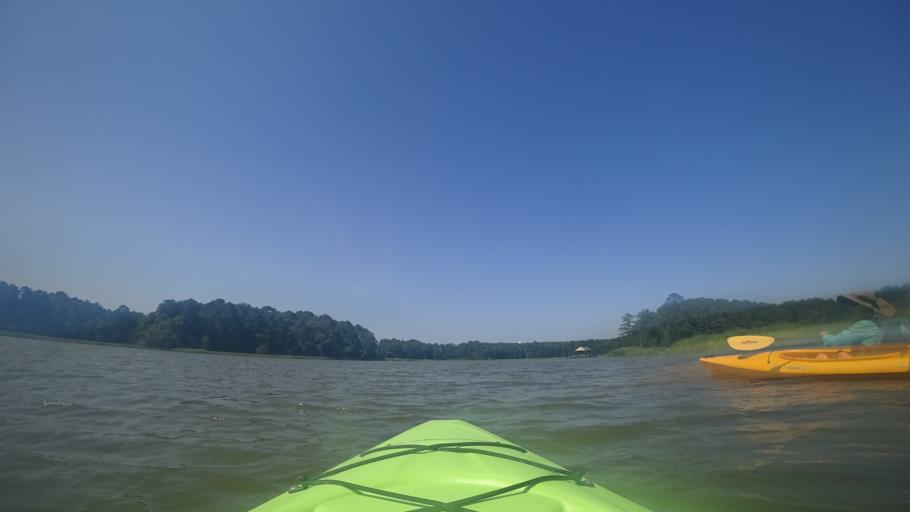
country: US
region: Virginia
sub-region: Isle of Wight County
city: Smithfield
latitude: 36.9560
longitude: -76.6167
